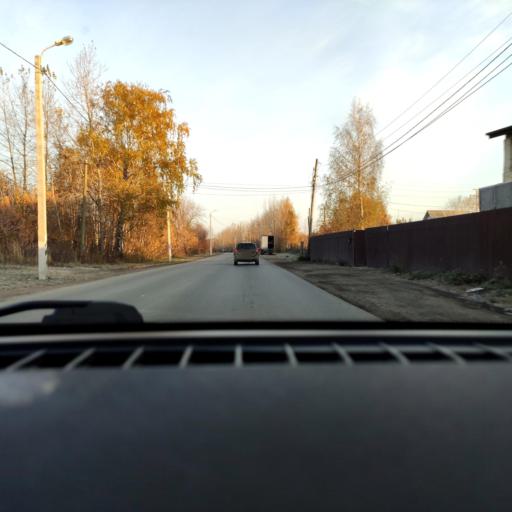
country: RU
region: Perm
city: Kondratovo
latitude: 57.9413
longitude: 56.1545
